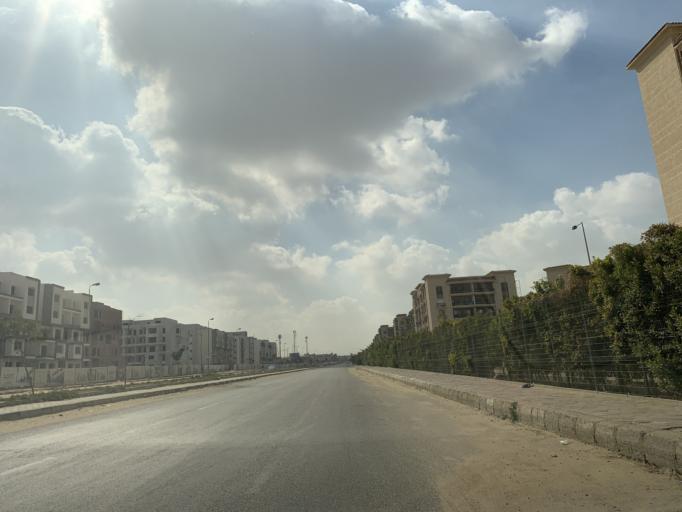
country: EG
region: Muhafazat al Qalyubiyah
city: Al Khankah
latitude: 30.0673
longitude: 31.5199
